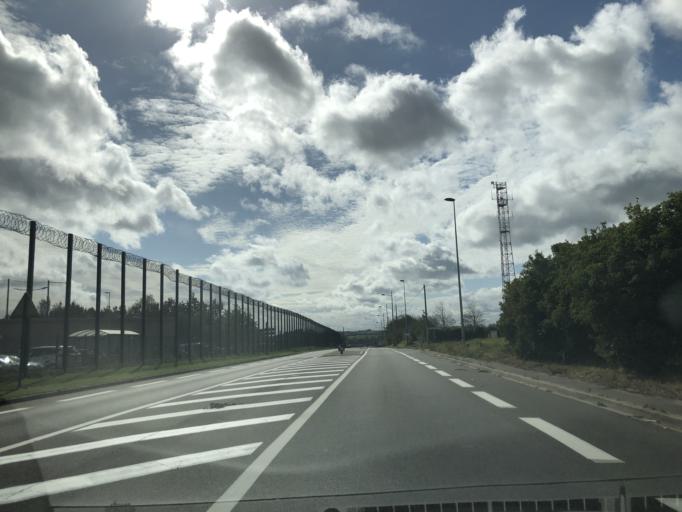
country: FR
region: Nord-Pas-de-Calais
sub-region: Departement du Pas-de-Calais
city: Longuenesse
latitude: 50.7270
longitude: 2.2462
